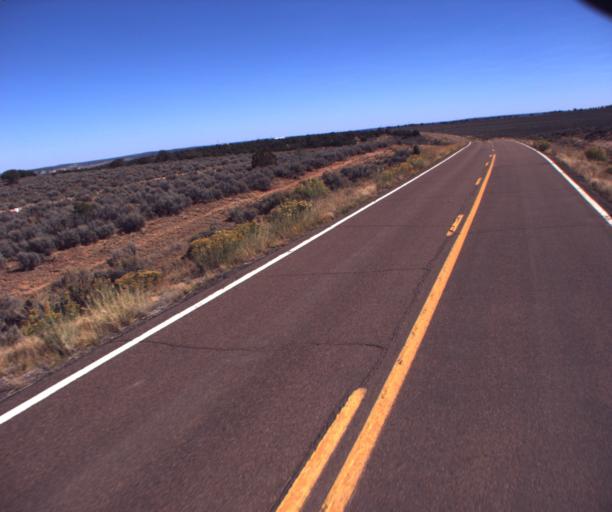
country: US
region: Arizona
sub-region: Apache County
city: Ganado
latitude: 35.7494
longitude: -109.9358
